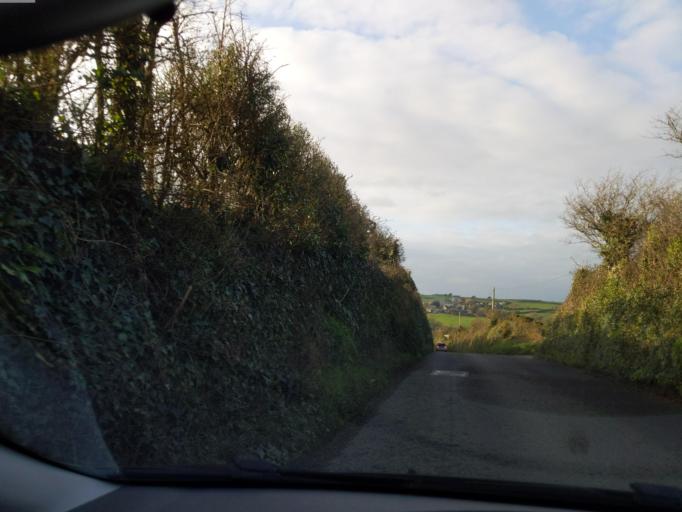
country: GB
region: England
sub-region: Cornwall
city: Padstow
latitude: 50.5110
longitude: -4.9294
